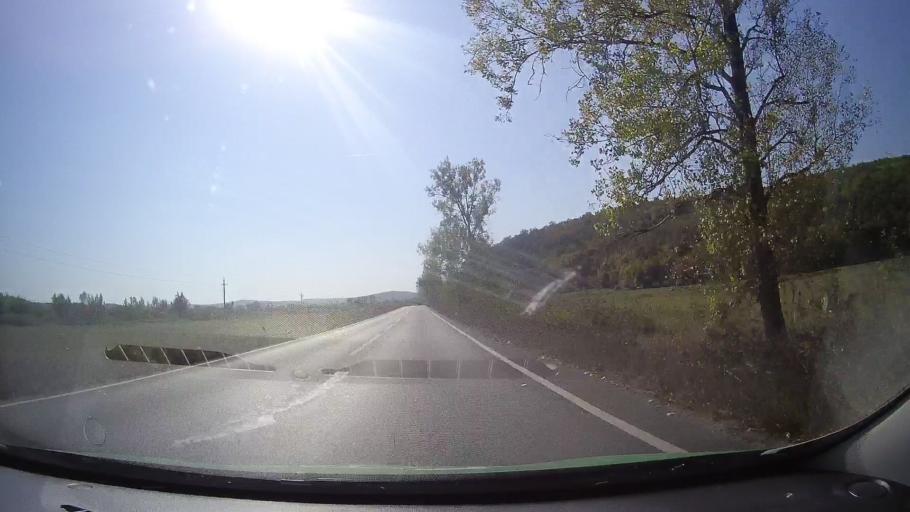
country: RO
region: Arad
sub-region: Comuna Ususau
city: Ususau
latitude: 46.0999
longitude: 21.8145
